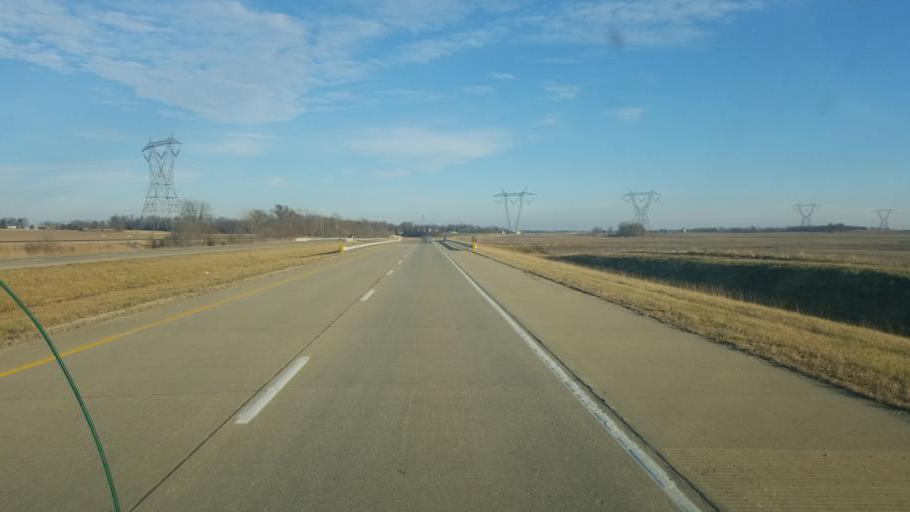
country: US
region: Indiana
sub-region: Knox County
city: Bicknell
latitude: 38.6687
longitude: -87.3374
